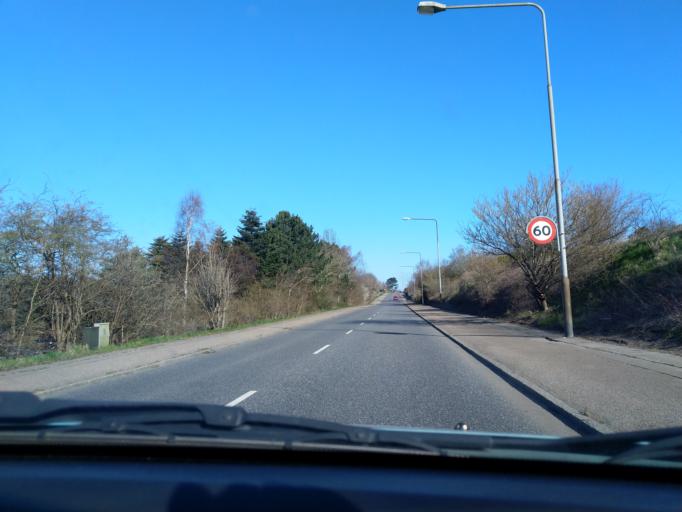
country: DK
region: Zealand
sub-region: Kalundborg Kommune
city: Kalundborg
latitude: 55.7051
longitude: 11.0236
